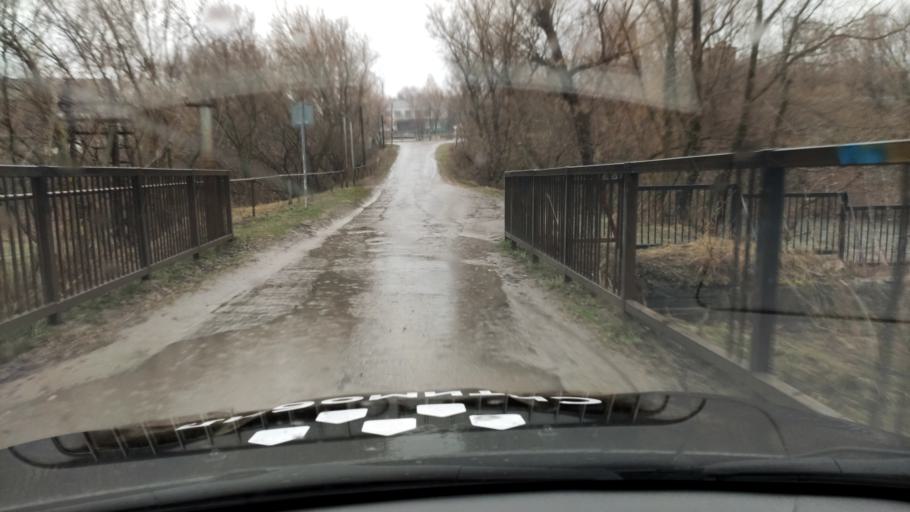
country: RU
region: Samara
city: Balasheyka
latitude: 53.2293
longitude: 48.2347
